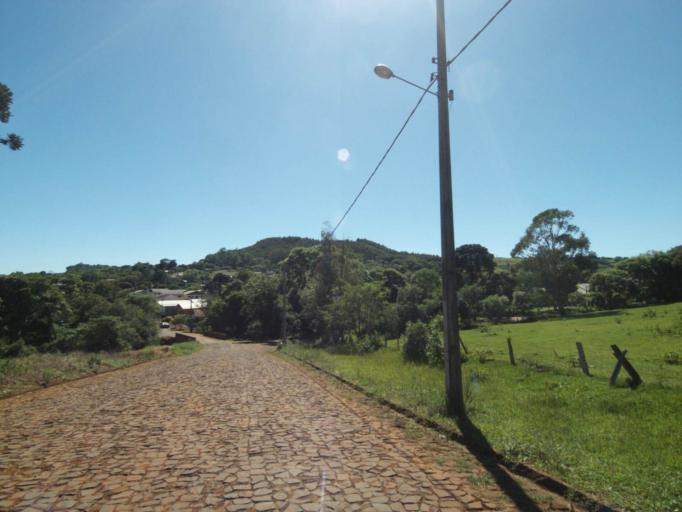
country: BR
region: Santa Catarina
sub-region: Sao Lourenco Do Oeste
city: Sao Lourenco dOeste
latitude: -26.2702
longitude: -52.7795
